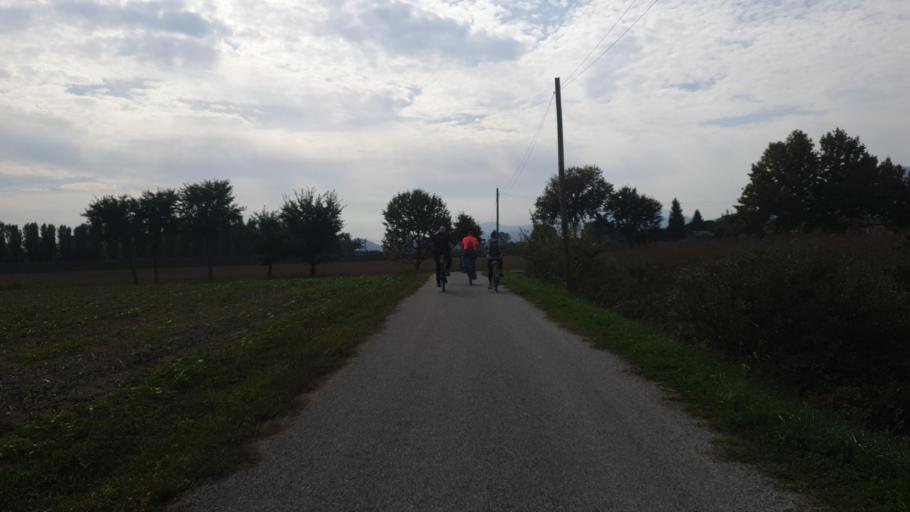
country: IT
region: Veneto
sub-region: Provincia di Padova
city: Cervarese Santa Croce
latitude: 45.4062
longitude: 11.6964
